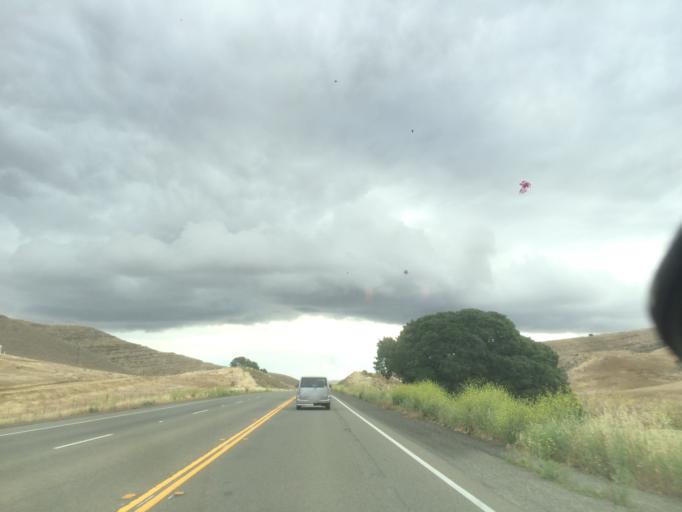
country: US
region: California
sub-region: Kings County
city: Avenal
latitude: 35.7726
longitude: -120.1642
